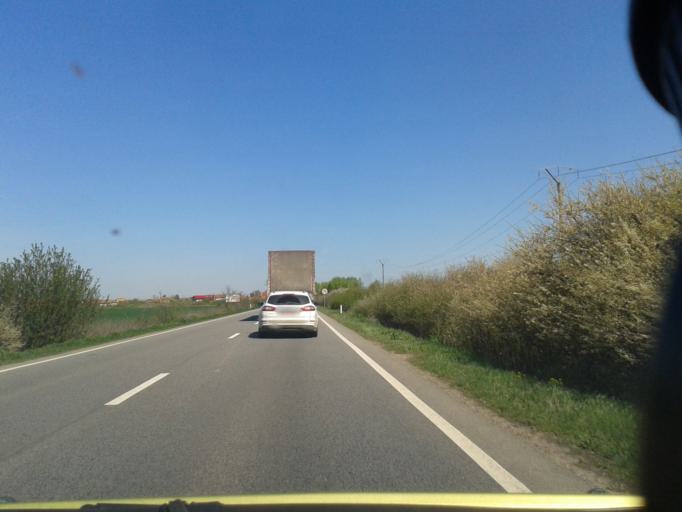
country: RO
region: Bihor
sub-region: Comuna Cefa
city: Cefa
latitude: 46.8874
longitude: 21.7496
